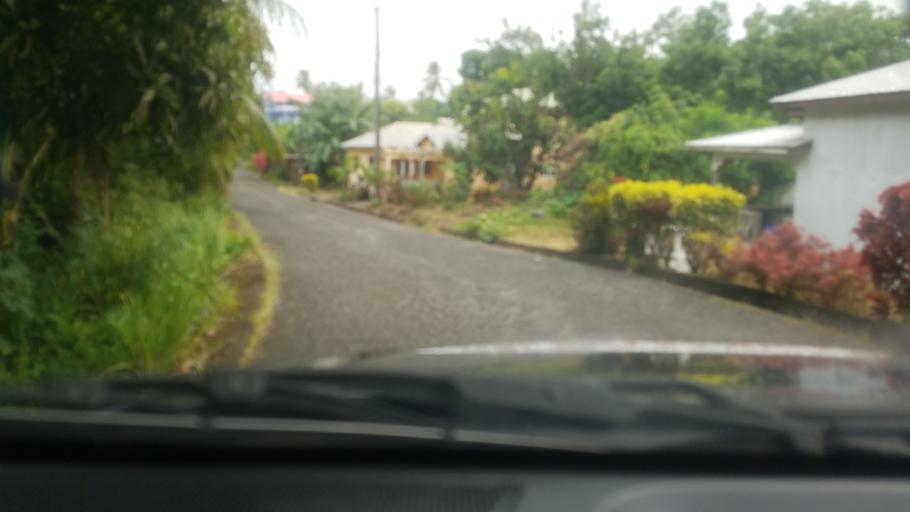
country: LC
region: Micoud Quarter
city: Micoud
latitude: 13.8097
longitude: -60.9486
